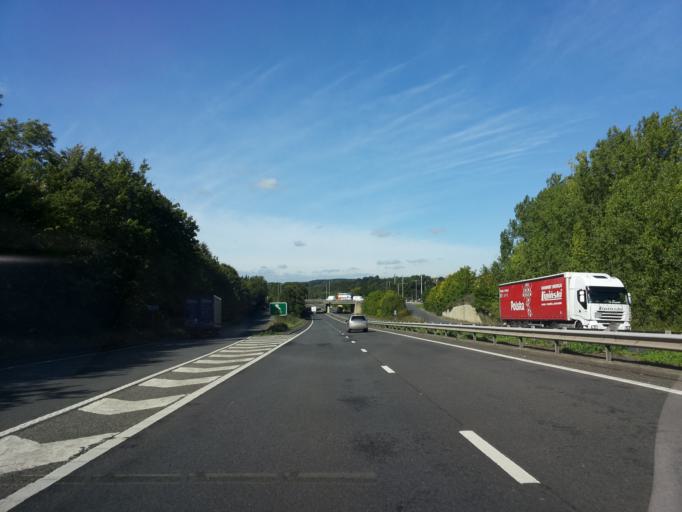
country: GB
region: England
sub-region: Kent
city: Canterbury
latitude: 51.2676
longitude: 1.0650
